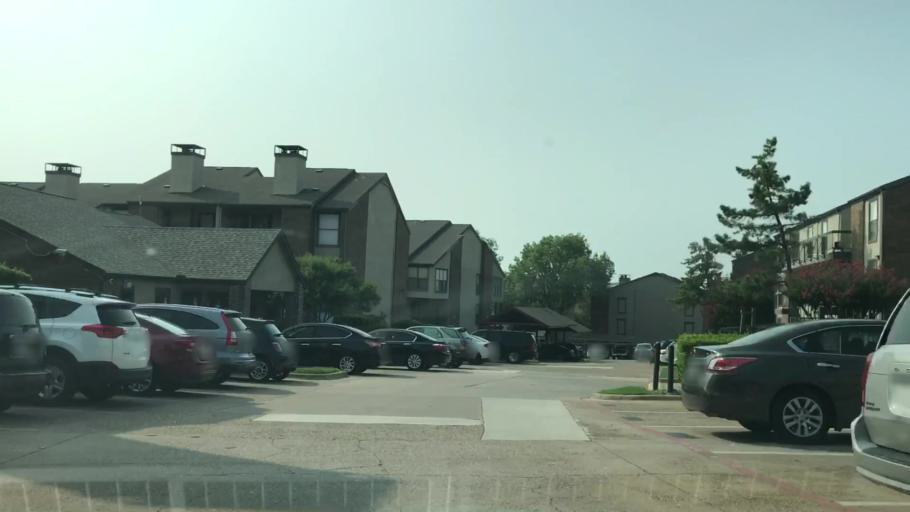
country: US
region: Texas
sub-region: Dallas County
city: Richardson
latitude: 32.9136
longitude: -96.7489
